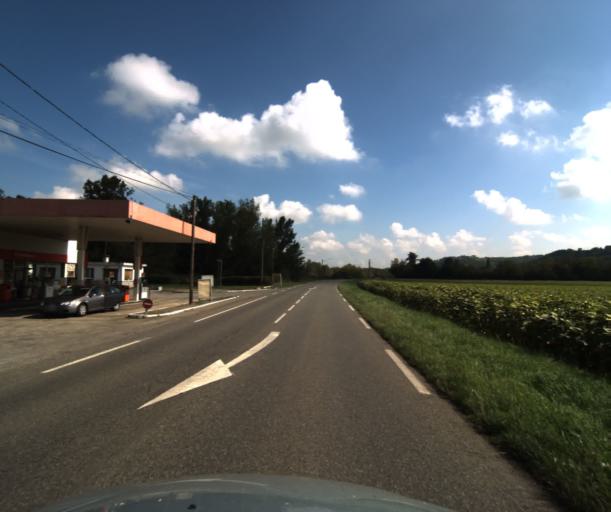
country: FR
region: Midi-Pyrenees
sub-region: Departement de la Haute-Garonne
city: Portet-sur-Garonne
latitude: 43.5178
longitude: 1.4181
